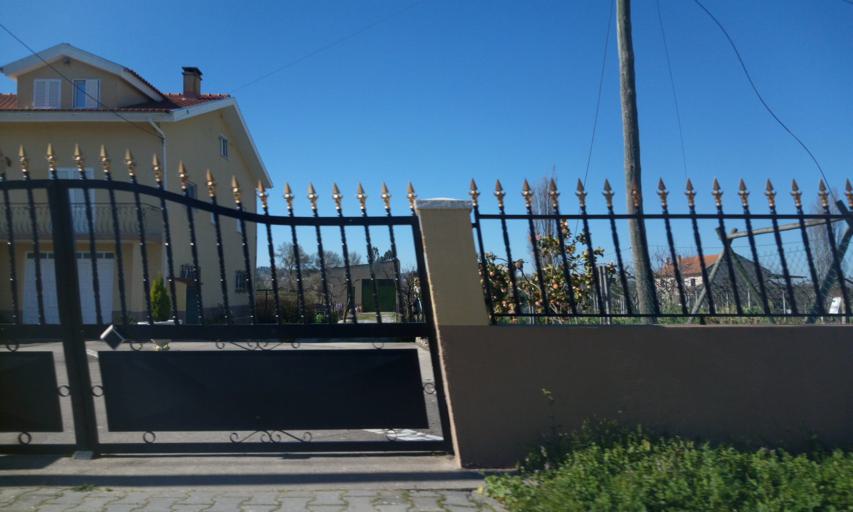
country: PT
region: Guarda
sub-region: Fornos de Algodres
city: Fornos de Algodres
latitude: 40.5324
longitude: -7.5606
